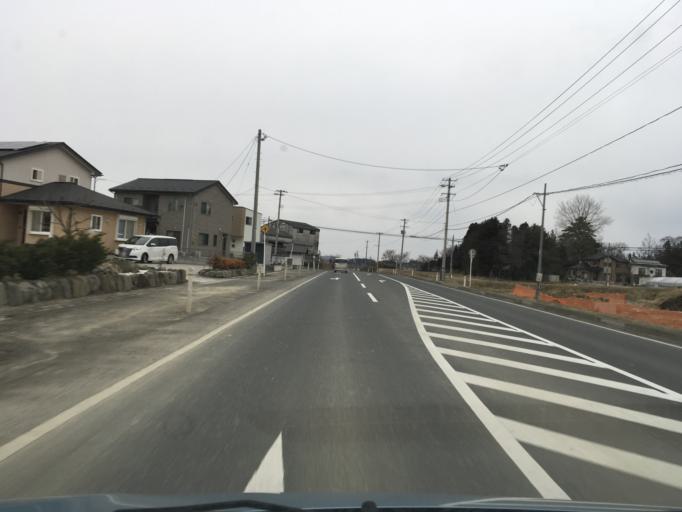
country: JP
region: Miyagi
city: Wakuya
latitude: 38.6737
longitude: 141.2702
